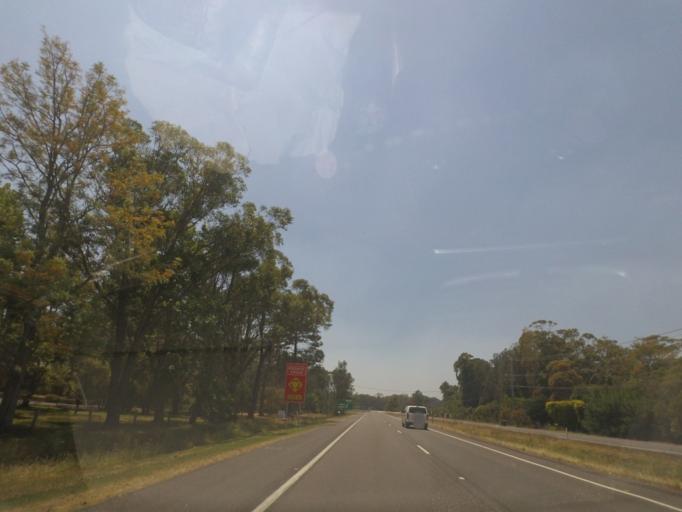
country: AU
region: New South Wales
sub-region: Port Stephens Shire
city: Medowie
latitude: -32.7911
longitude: 151.9000
